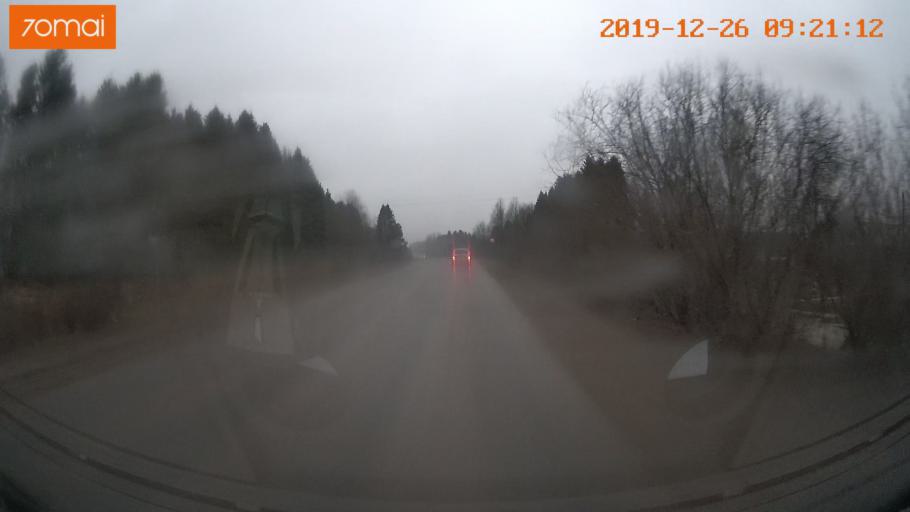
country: RU
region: Vologda
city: Gryazovets
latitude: 58.9684
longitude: 40.2257
